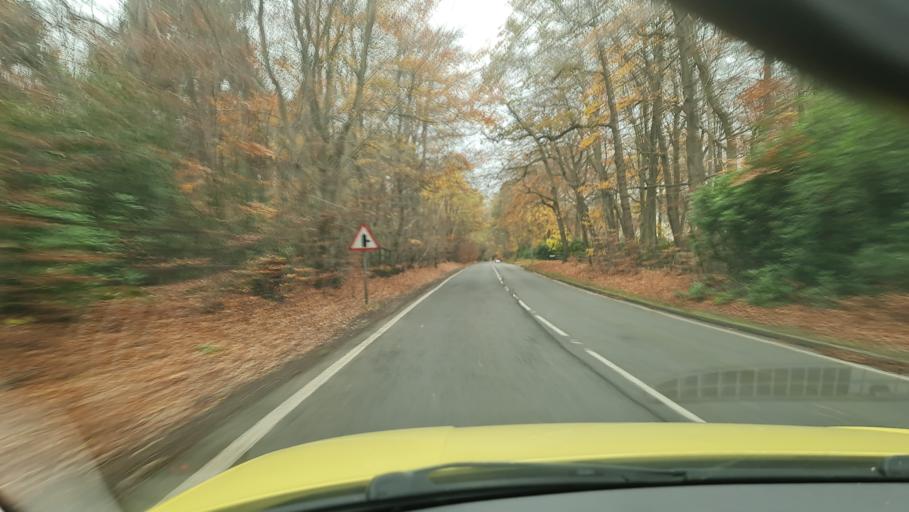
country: GB
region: England
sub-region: Bracknell Forest
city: Sandhurst
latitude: 51.3213
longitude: -0.7815
